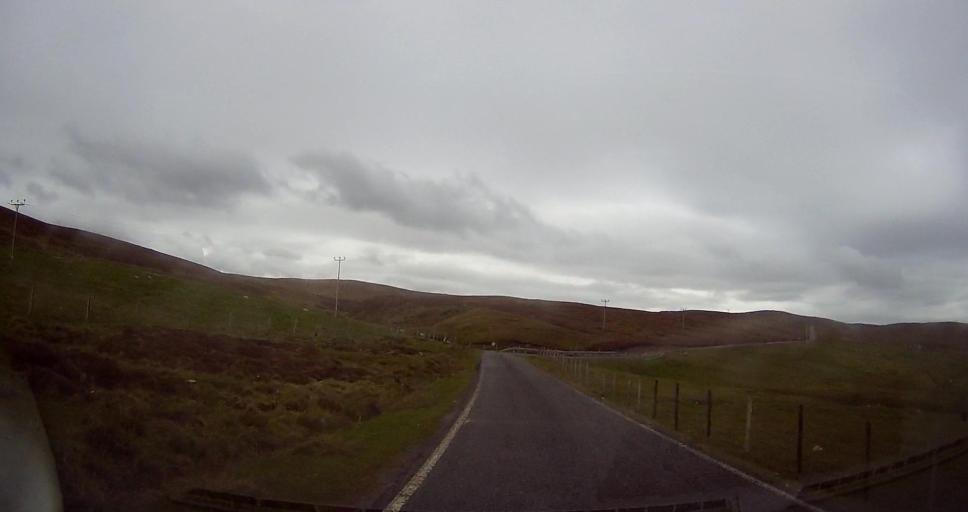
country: GB
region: Scotland
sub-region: Shetland Islands
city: Lerwick
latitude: 60.4924
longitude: -1.5489
